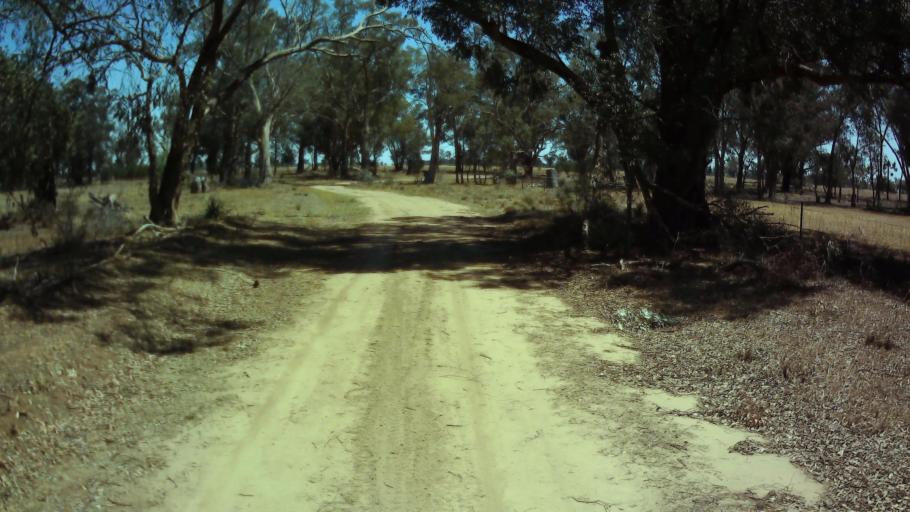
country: AU
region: New South Wales
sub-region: Weddin
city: Grenfell
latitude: -34.0346
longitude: 147.9278
